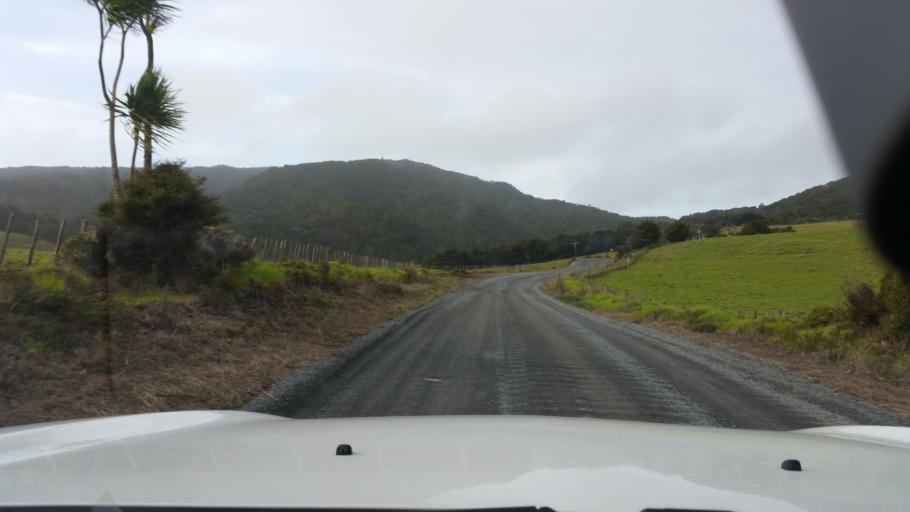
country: NZ
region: Northland
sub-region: Whangarei
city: Ngunguru
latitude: -35.7663
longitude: 174.5283
